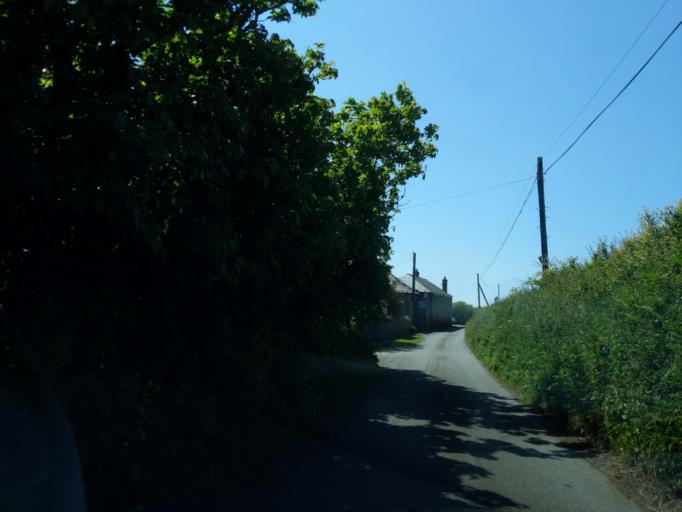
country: GB
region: England
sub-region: Cornwall
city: Wadebridge
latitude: 50.5840
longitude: -4.8465
